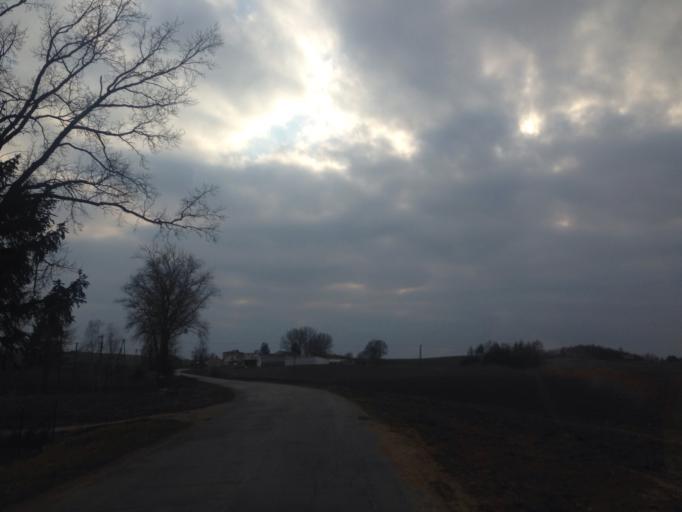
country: PL
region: Warmian-Masurian Voivodeship
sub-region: Powiat dzialdowski
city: Lidzbark
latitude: 53.3554
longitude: 19.7622
